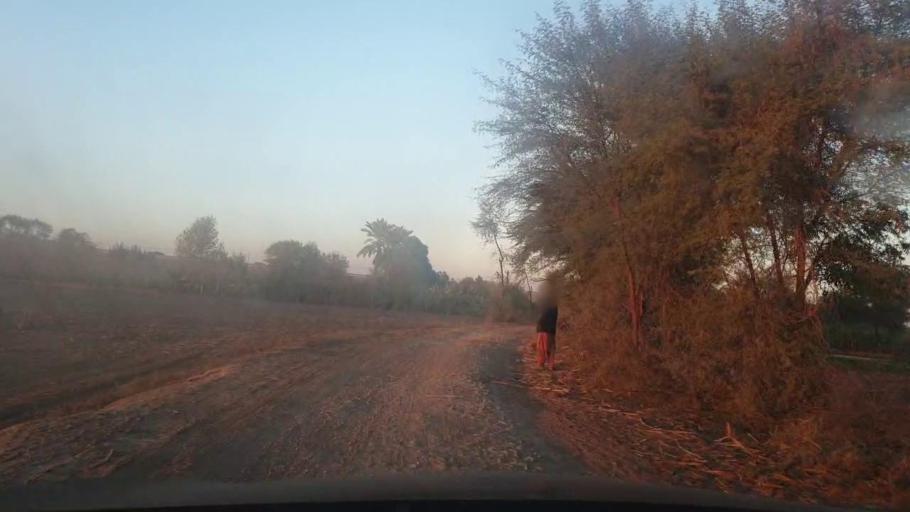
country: PK
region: Sindh
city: Ghotki
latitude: 28.0585
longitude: 69.3677
